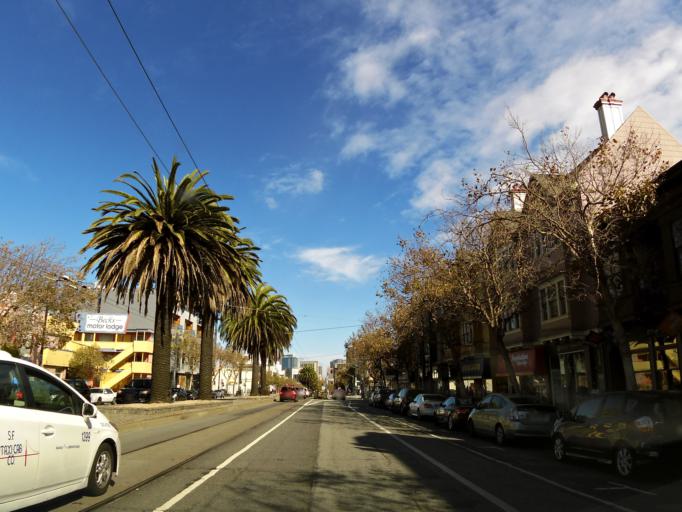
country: US
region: California
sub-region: San Francisco County
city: San Francisco
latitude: 37.7649
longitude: -122.4321
